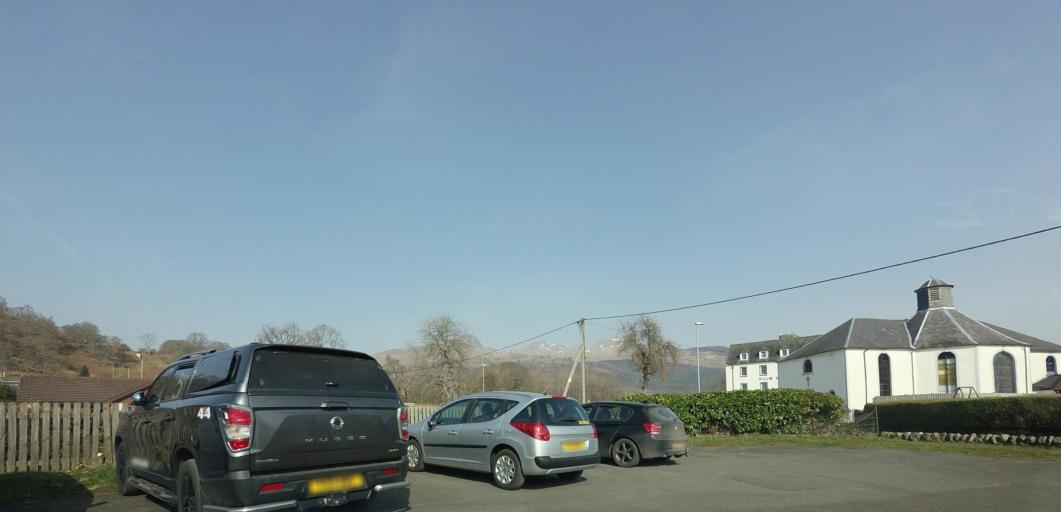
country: GB
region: Scotland
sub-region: Stirling
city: Callander
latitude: 56.4692
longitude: -4.3178
